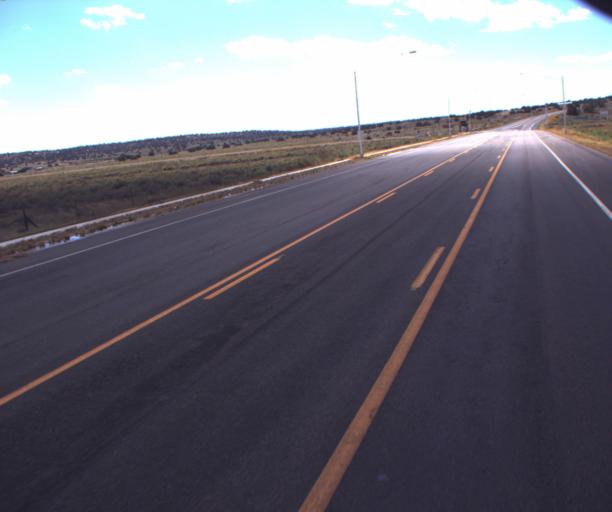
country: US
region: Arizona
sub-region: Apache County
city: Houck
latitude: 35.1997
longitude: -109.3327
